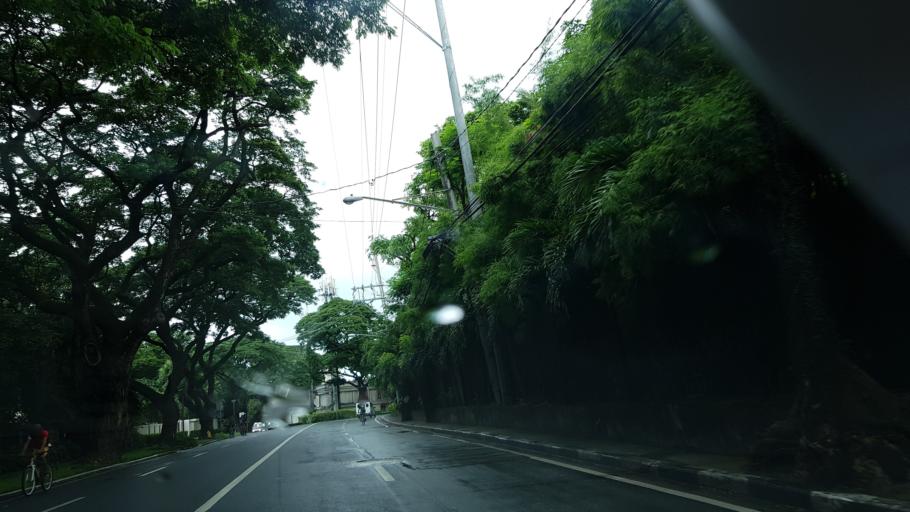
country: PH
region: Metro Manila
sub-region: Makati City
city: Makati City
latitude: 14.5474
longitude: 121.0367
